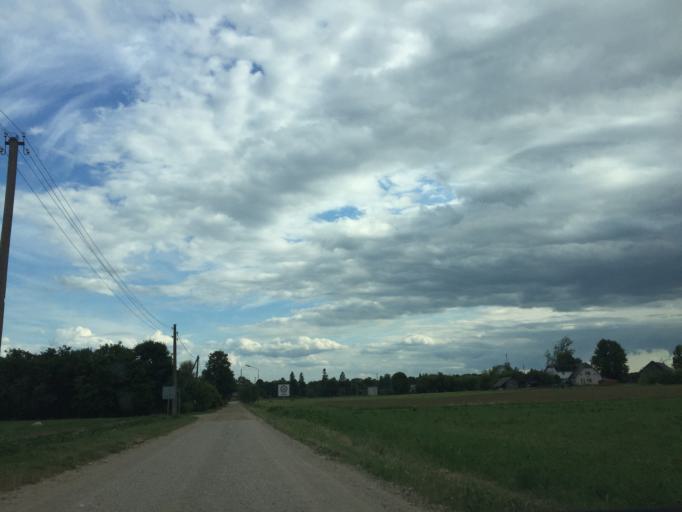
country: LV
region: Pargaujas
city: Stalbe
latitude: 57.3603
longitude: 24.9498
